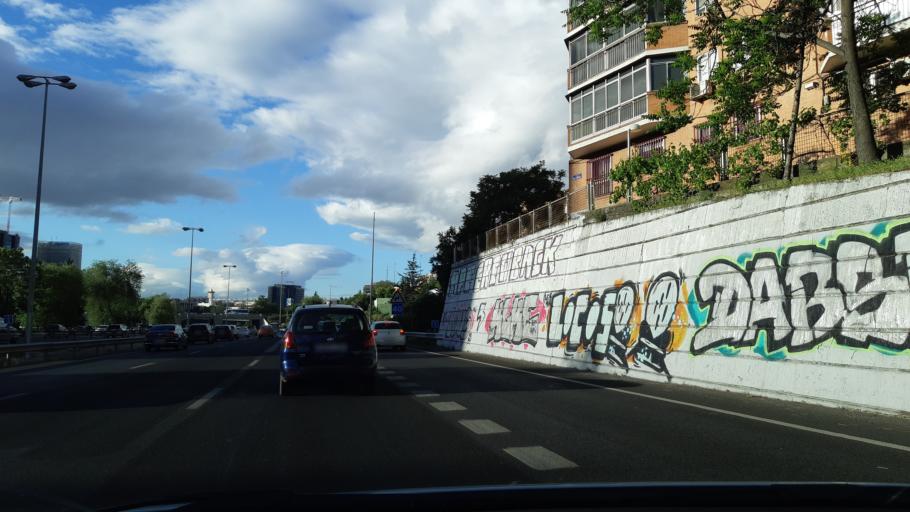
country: ES
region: Madrid
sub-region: Provincia de Madrid
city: Ciudad Lineal
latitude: 40.4478
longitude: -3.6624
